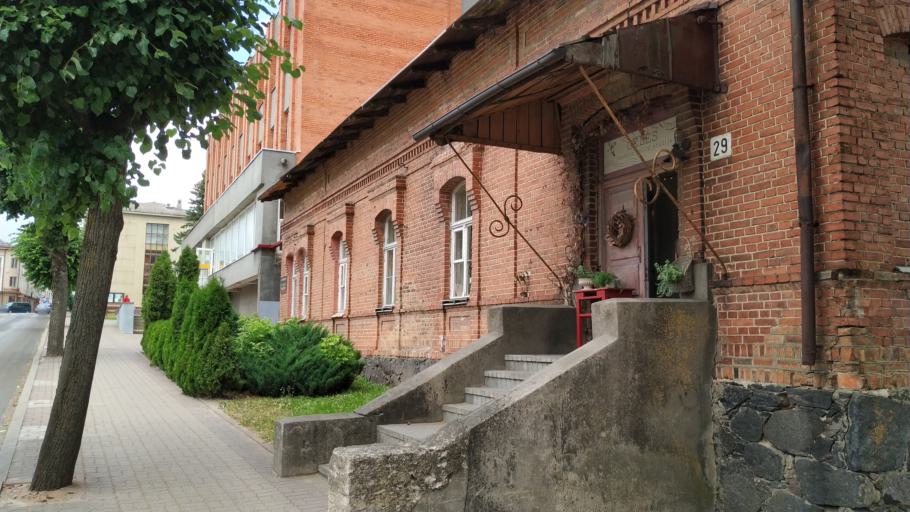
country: LT
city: Kupiskis
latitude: 55.8379
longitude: 24.9769
